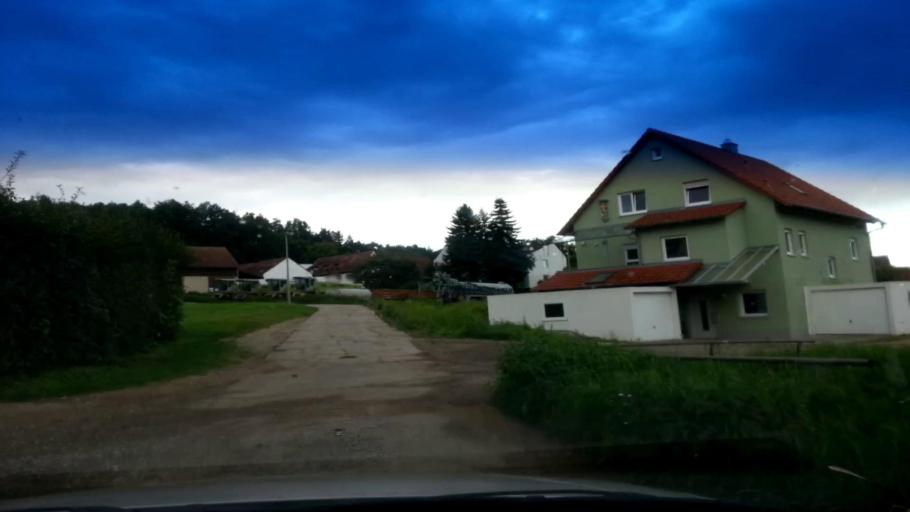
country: DE
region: Bavaria
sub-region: Upper Franconia
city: Gundelsheim
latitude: 49.9678
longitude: 10.9259
